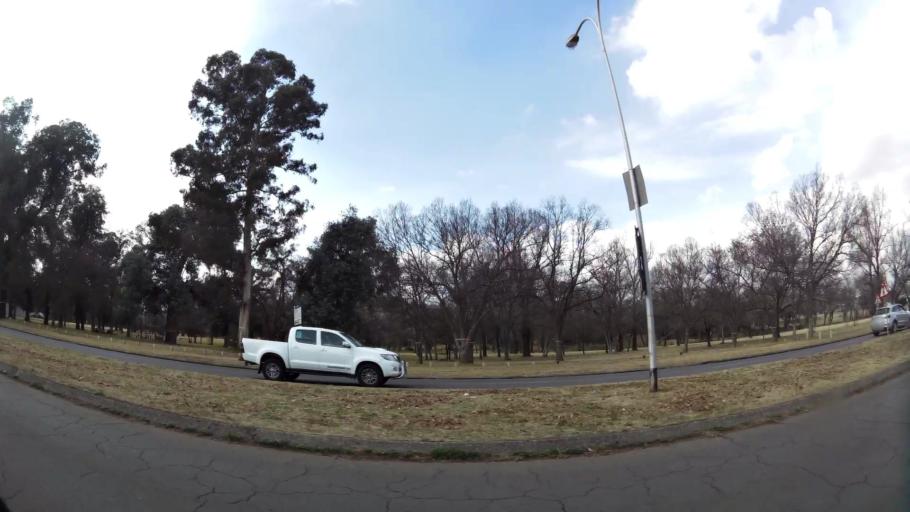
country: ZA
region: Gauteng
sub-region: Sedibeng District Municipality
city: Vanderbijlpark
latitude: -26.7313
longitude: 27.8374
